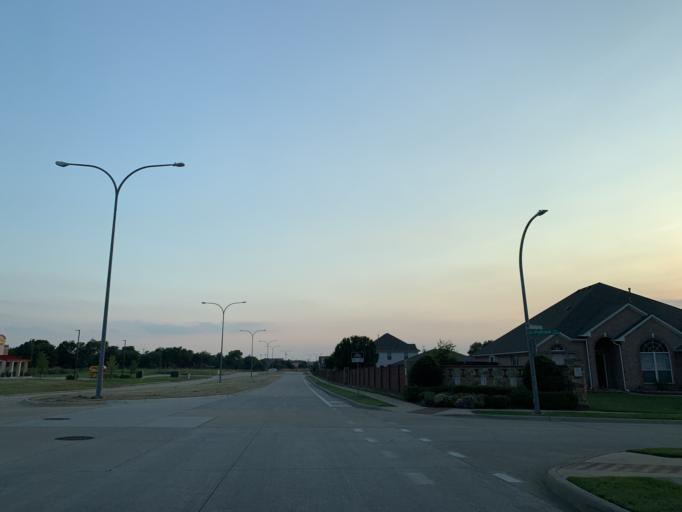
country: US
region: Texas
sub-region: Tarrant County
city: Keller
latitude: 32.9553
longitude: -97.2762
